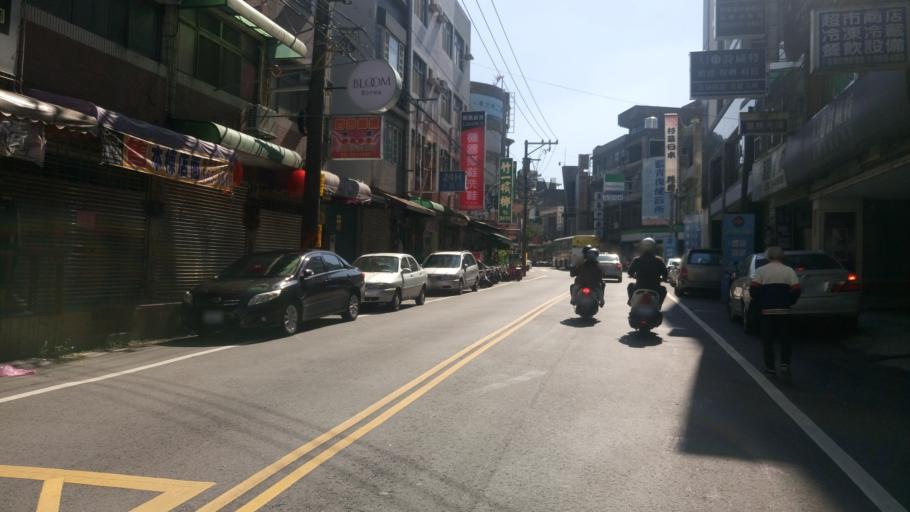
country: TW
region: Taiwan
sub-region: Hsinchu
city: Zhubei
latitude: 24.7407
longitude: 121.0854
